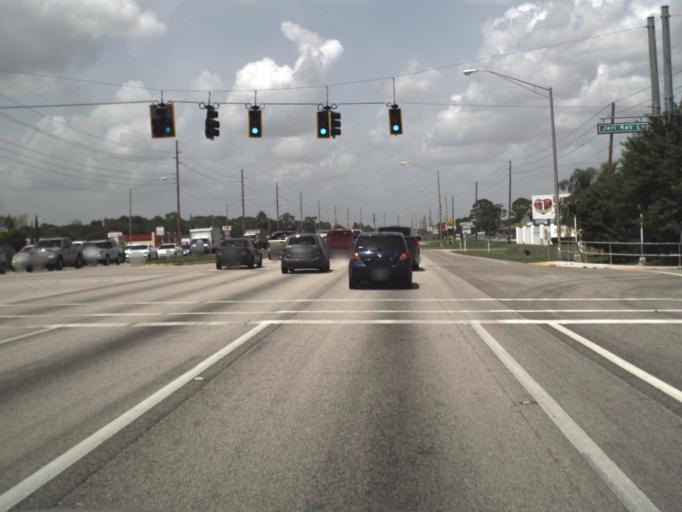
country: US
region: Florida
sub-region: Highlands County
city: Sebring
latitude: 27.4932
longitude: -81.4853
